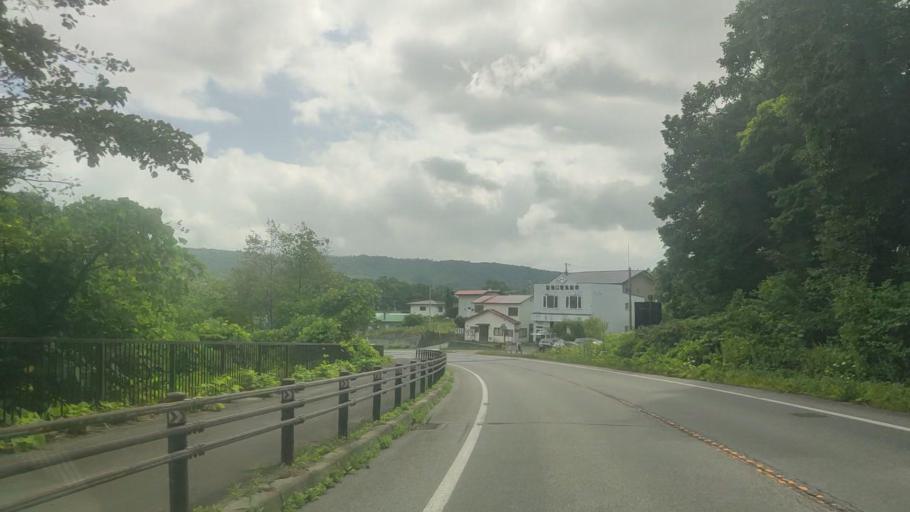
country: JP
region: Hokkaido
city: Date
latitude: 42.5591
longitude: 140.8863
